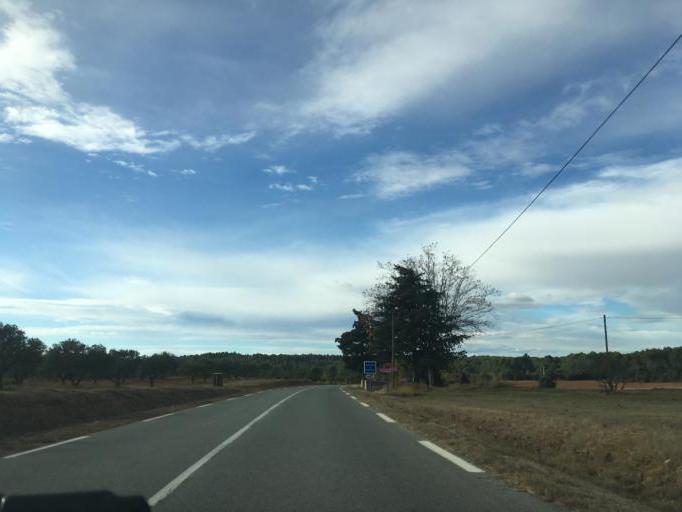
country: FR
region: Provence-Alpes-Cote d'Azur
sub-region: Departement du Var
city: Villecroze
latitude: 43.5983
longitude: 6.2466
